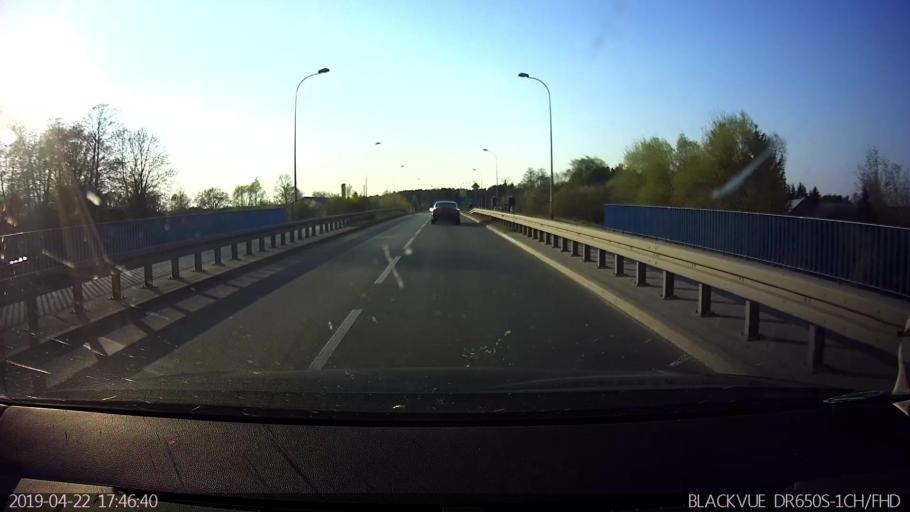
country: PL
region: Masovian Voivodeship
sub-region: Powiat wegrowski
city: Wegrow
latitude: 52.4025
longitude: 22.0252
